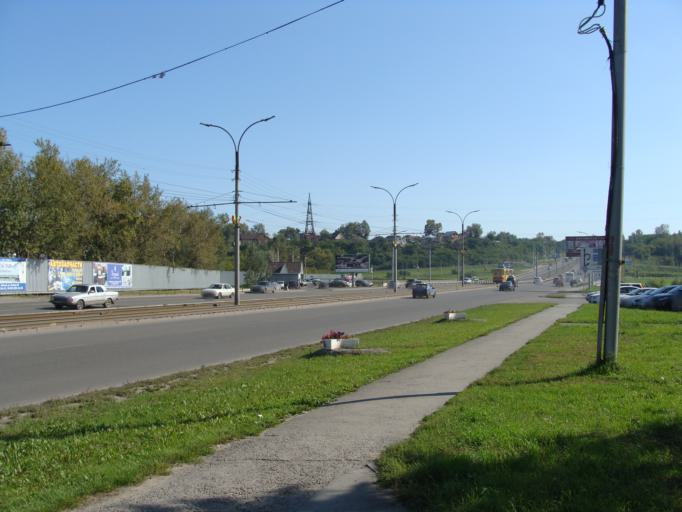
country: RU
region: Altai Krai
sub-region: Gorod Barnaulskiy
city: Barnaul
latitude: 53.3273
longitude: 83.7855
